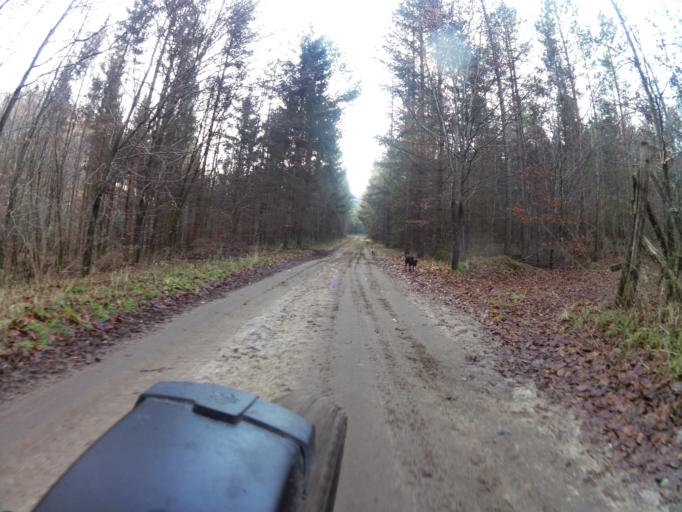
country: PL
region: West Pomeranian Voivodeship
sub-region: Powiat koszalinski
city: Polanow
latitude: 54.1842
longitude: 16.7197
